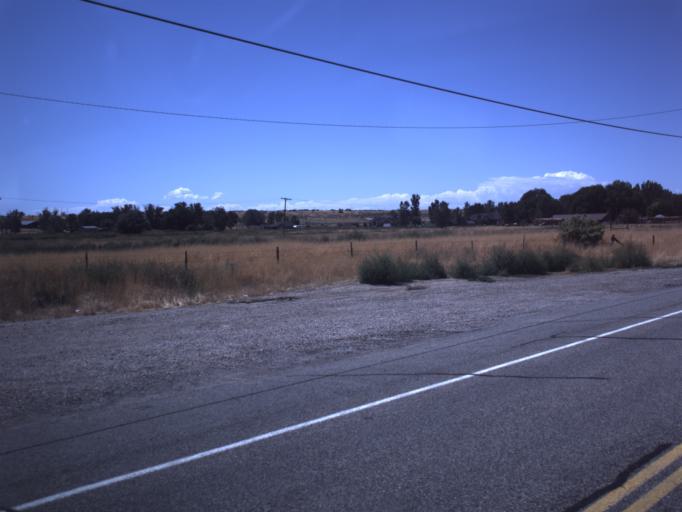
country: US
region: Utah
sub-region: Millard County
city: Delta
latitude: 39.5340
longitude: -112.2916
